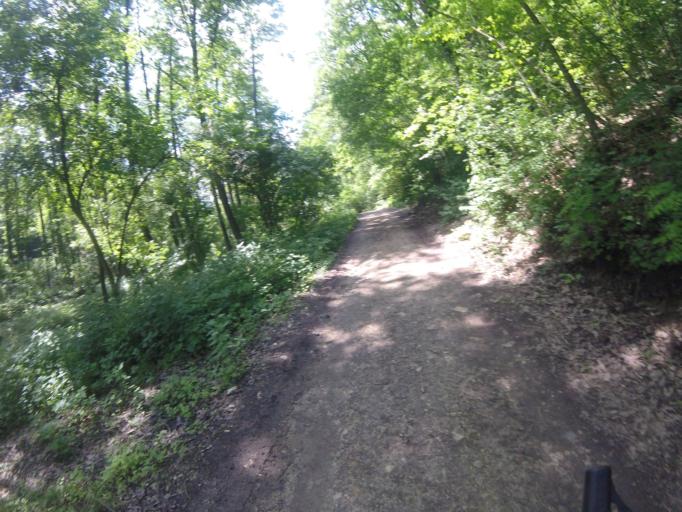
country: HU
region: Veszprem
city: Cseteny
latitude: 47.2716
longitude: 17.9981
